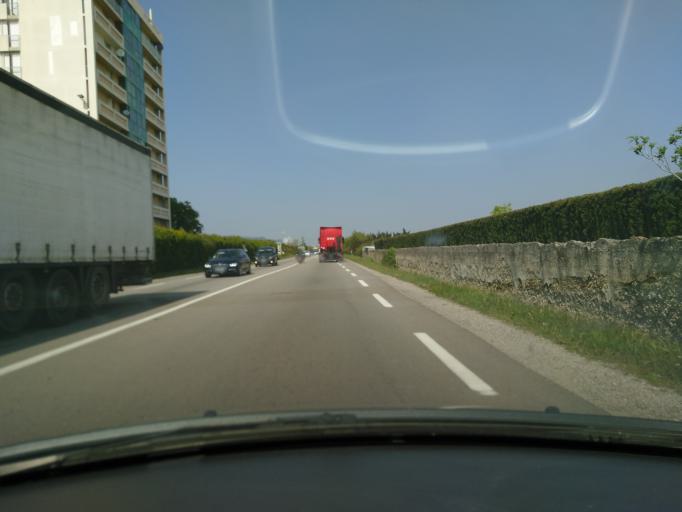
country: FR
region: Rhone-Alpes
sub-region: Departement de la Drome
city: Montelimar
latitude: 44.5590
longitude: 4.7297
